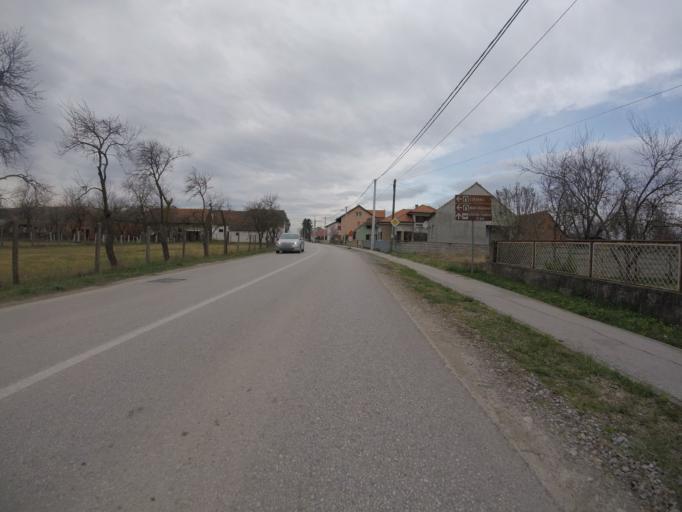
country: HR
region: Zagrebacka
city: Gradici
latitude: 45.7148
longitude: 16.0247
